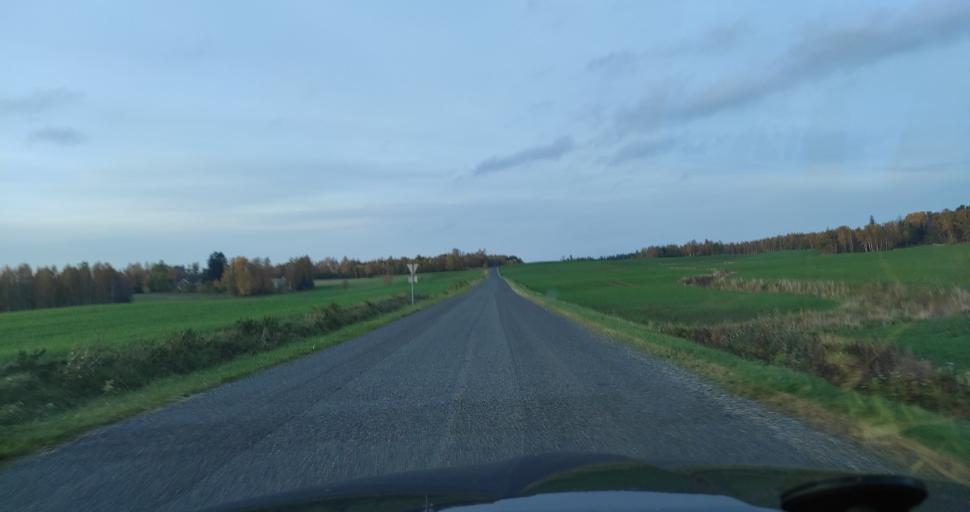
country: LV
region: Aizpute
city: Aizpute
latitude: 56.7004
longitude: 21.7953
